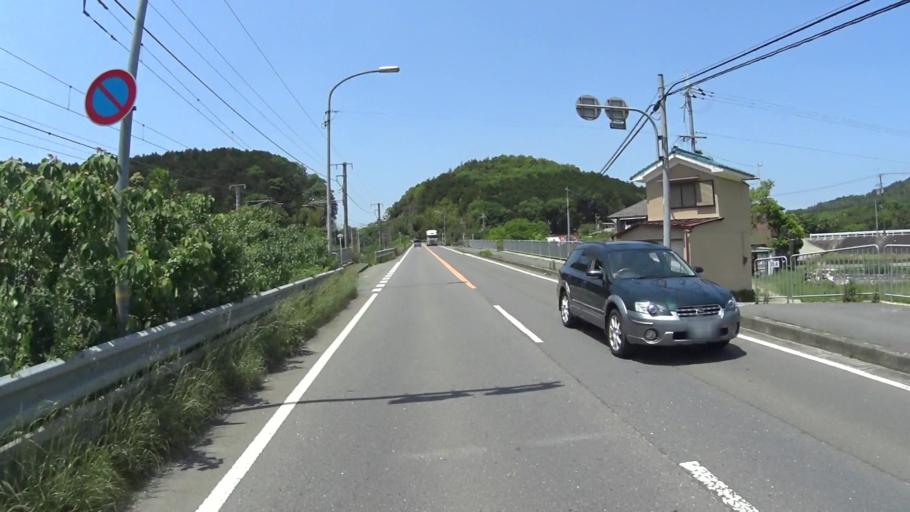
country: JP
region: Kyoto
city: Kameoka
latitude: 35.0793
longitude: 135.5181
